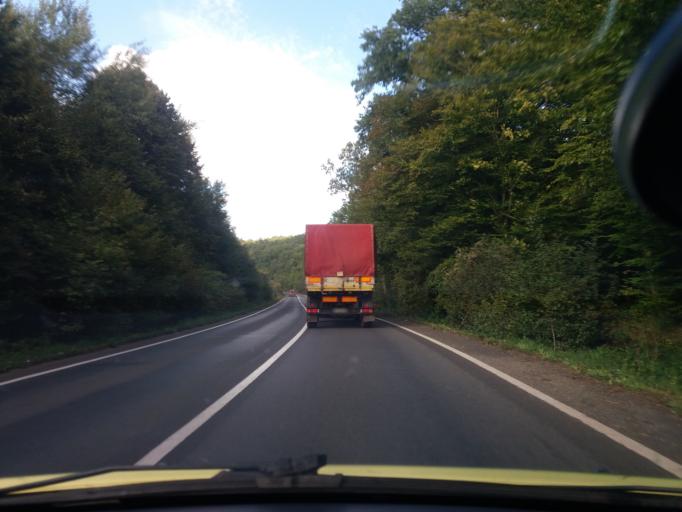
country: RO
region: Arad
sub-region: Comuna Ususau
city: Ususau
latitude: 46.0976
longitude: 21.7893
